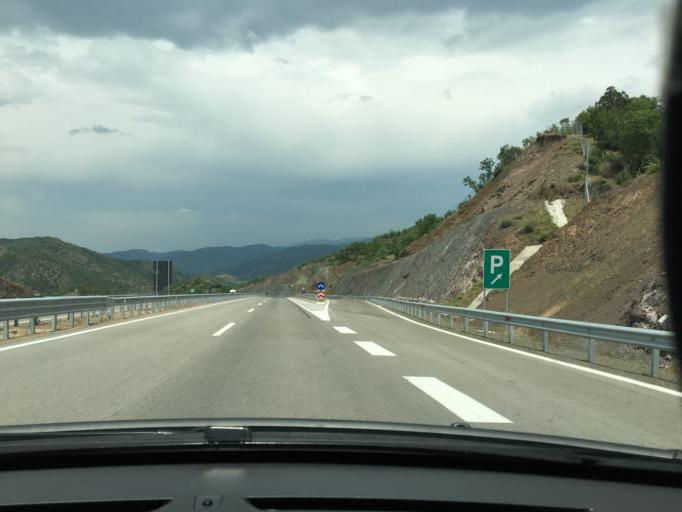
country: MK
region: Demir Kapija
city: Demir Kapija
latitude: 41.3630
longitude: 22.3453
